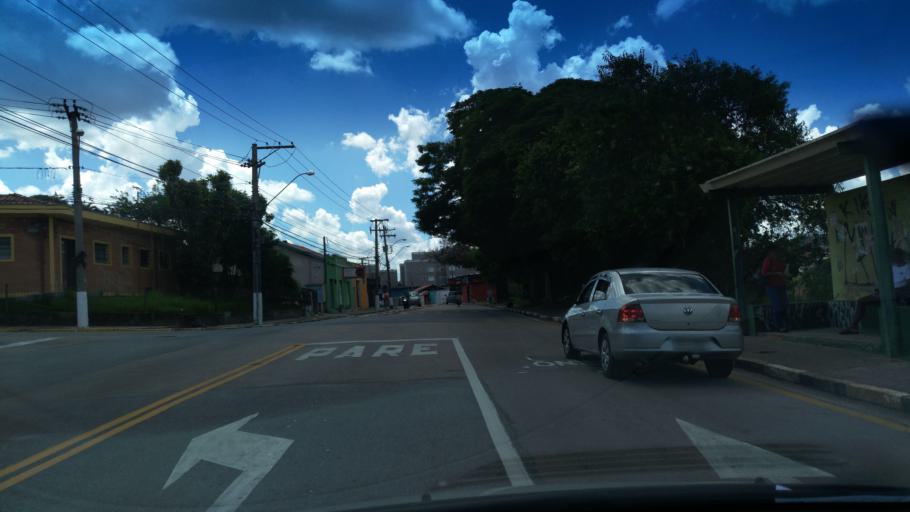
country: BR
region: Sao Paulo
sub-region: Vinhedo
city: Vinhedo
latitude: -23.0201
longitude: -46.9824
